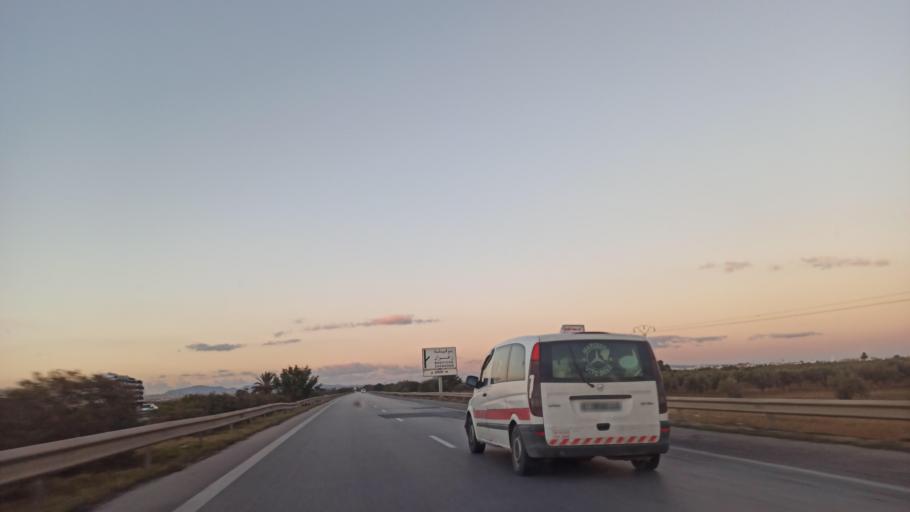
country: TN
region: Nabul
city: Al Hammamat
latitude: 36.2855
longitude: 10.4378
